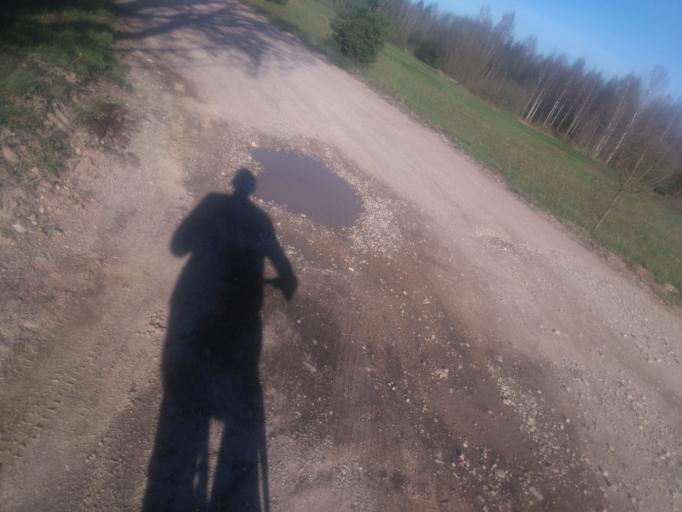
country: LV
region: Vecpiebalga
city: Vecpiebalga
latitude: 57.0175
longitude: 25.8341
